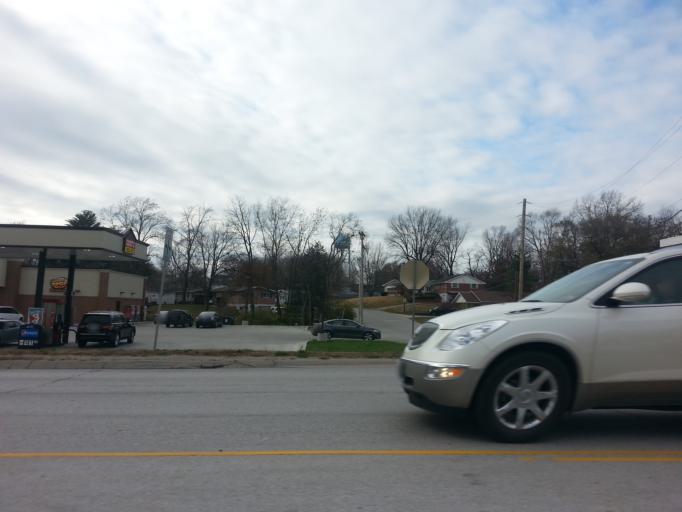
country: US
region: Missouri
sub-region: Marion County
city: Hannibal
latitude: 39.7188
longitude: -91.3920
